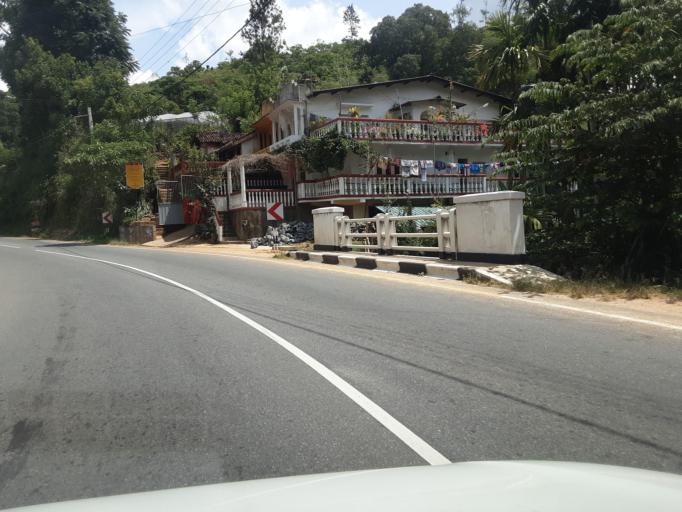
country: LK
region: Central
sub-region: Nuwara Eliya District
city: Nuwara Eliya
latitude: 6.9150
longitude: 80.9084
